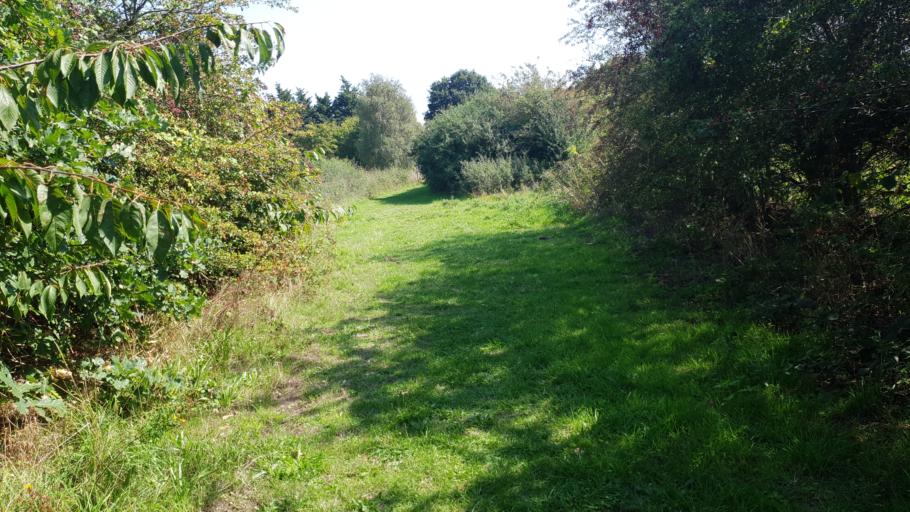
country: GB
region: England
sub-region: Essex
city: Wivenhoe
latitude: 51.9233
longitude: 0.9707
